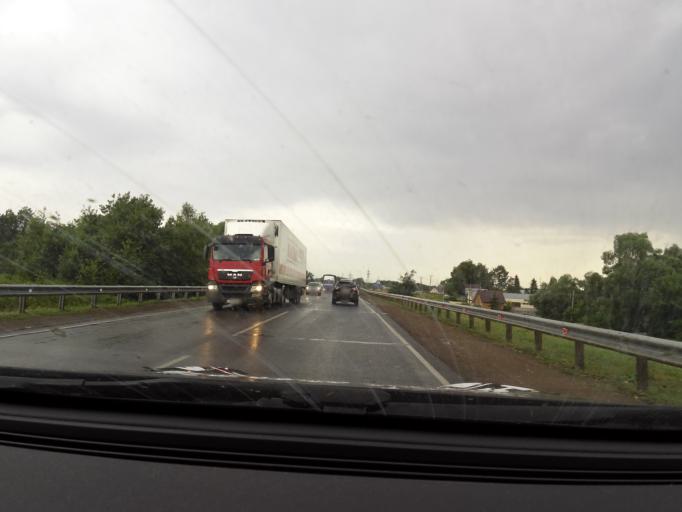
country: RU
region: Bashkortostan
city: Mikhaylovka
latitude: 54.8112
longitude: 55.8476
